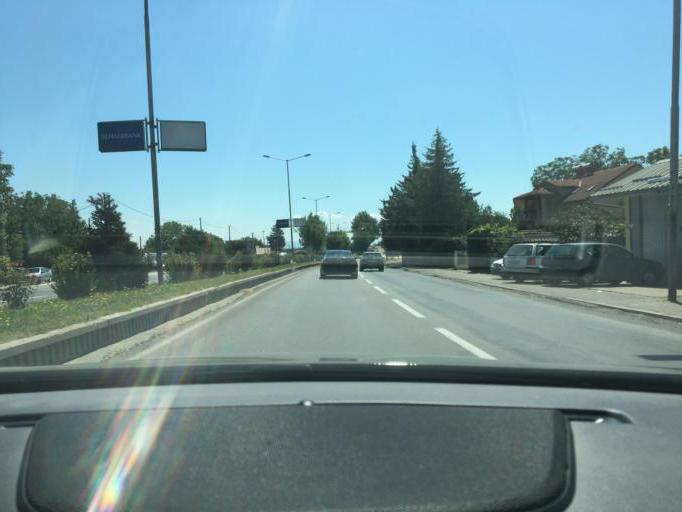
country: MK
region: Cair
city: Cair
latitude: 42.0039
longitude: 21.4837
